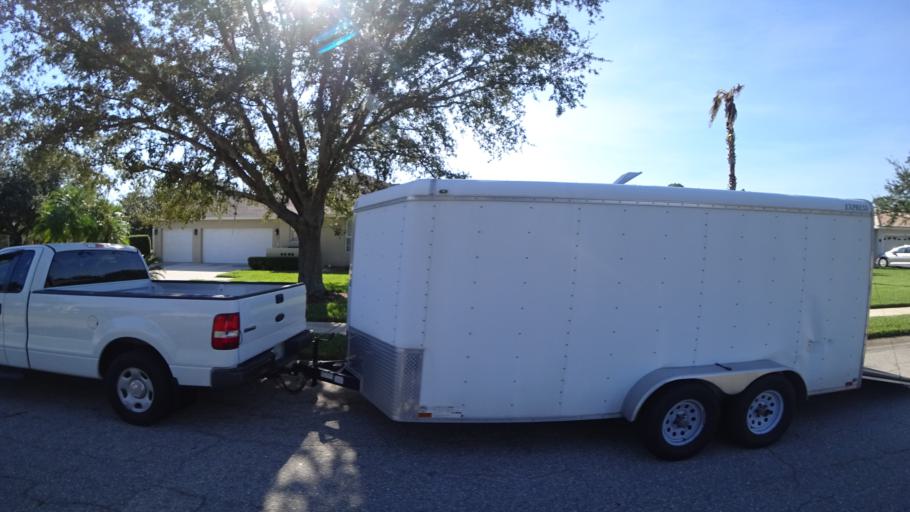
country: US
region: Florida
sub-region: Sarasota County
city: The Meadows
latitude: 27.4093
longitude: -82.4455
